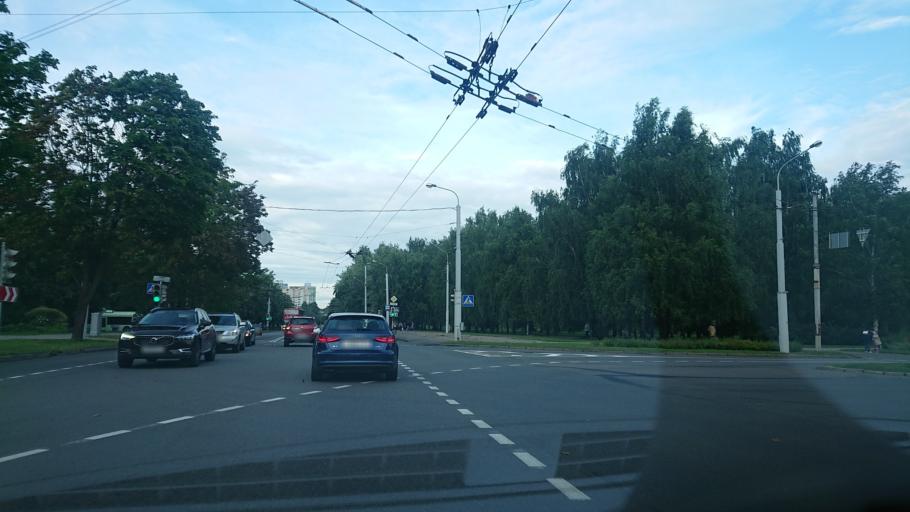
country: BY
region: Minsk
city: Borovlyany
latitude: 53.9352
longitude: 27.6362
